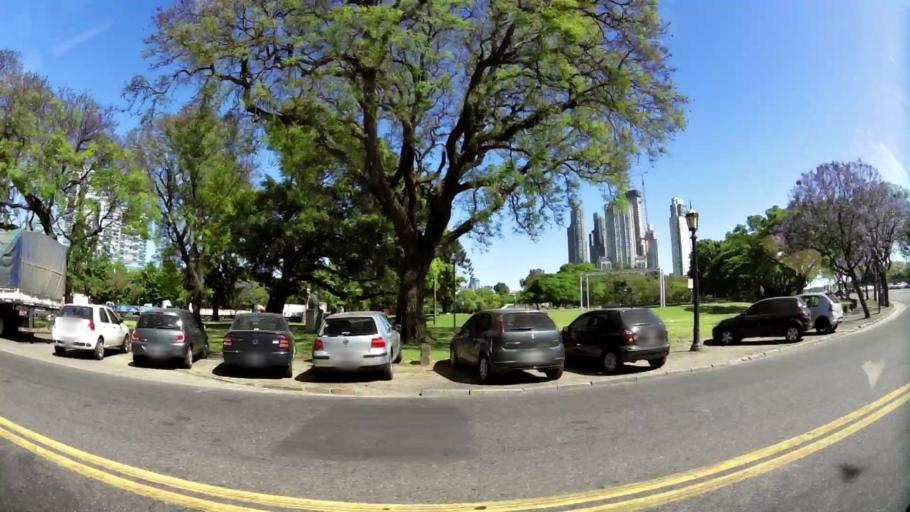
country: AR
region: Buenos Aires F.D.
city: Buenos Aires
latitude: -34.6184
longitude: -58.3567
